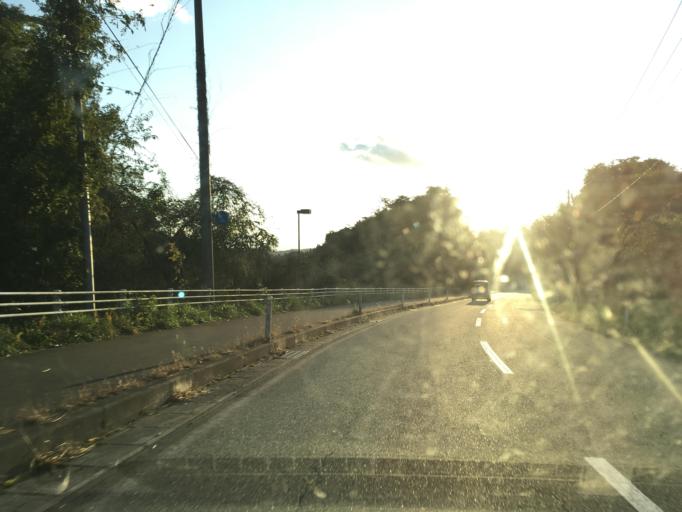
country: JP
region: Iwate
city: Ichinoseki
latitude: 38.9295
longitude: 141.3542
